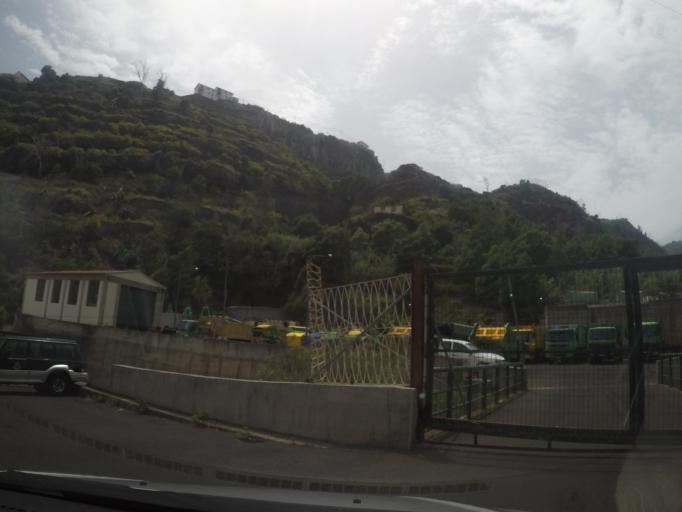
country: PT
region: Madeira
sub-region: Santa Cruz
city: Santa Cruz
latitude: 32.6860
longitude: -16.8011
